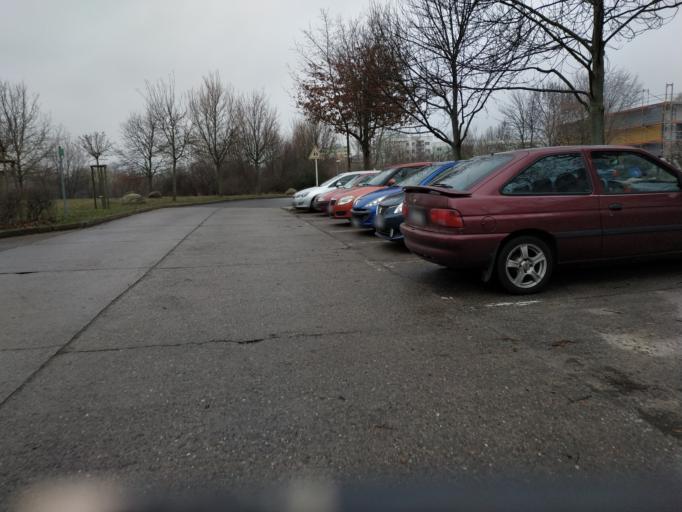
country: DE
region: Berlin
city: Marzahn
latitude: 52.5421
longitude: 13.5841
